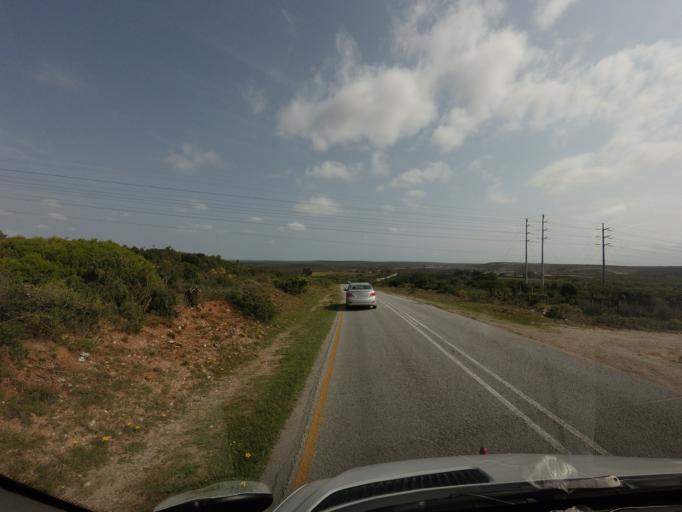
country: ZA
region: Eastern Cape
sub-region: Nelson Mandela Bay Metropolitan Municipality
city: Port Elizabeth
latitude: -33.7540
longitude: 25.5950
